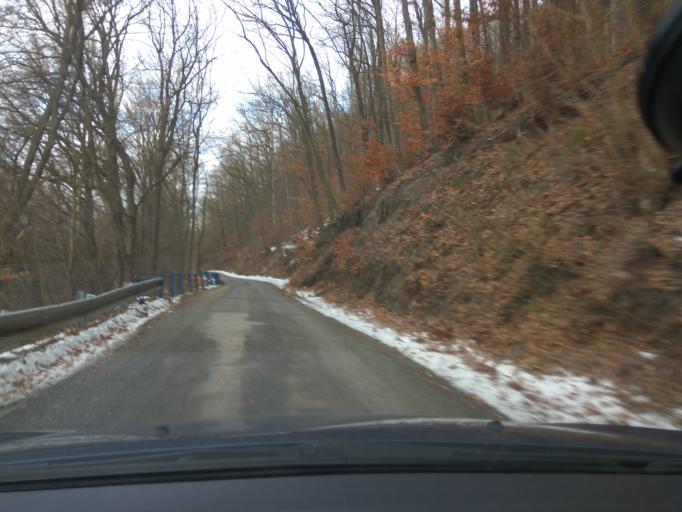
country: SK
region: Banskobystricky
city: Zarnovica
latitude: 48.4743
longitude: 18.7345
